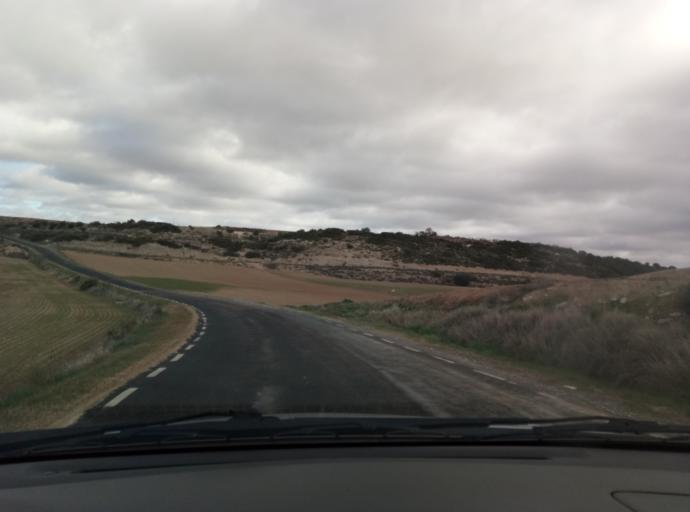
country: ES
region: Catalonia
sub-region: Provincia de Lleida
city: Nalec
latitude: 41.5861
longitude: 1.0839
